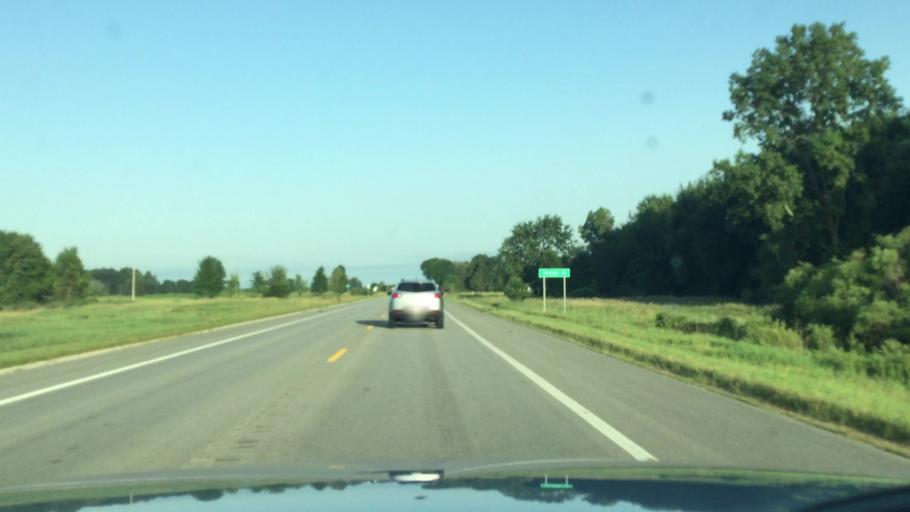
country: US
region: Michigan
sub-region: Montcalm County
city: Carson City
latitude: 43.1762
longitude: -84.7353
